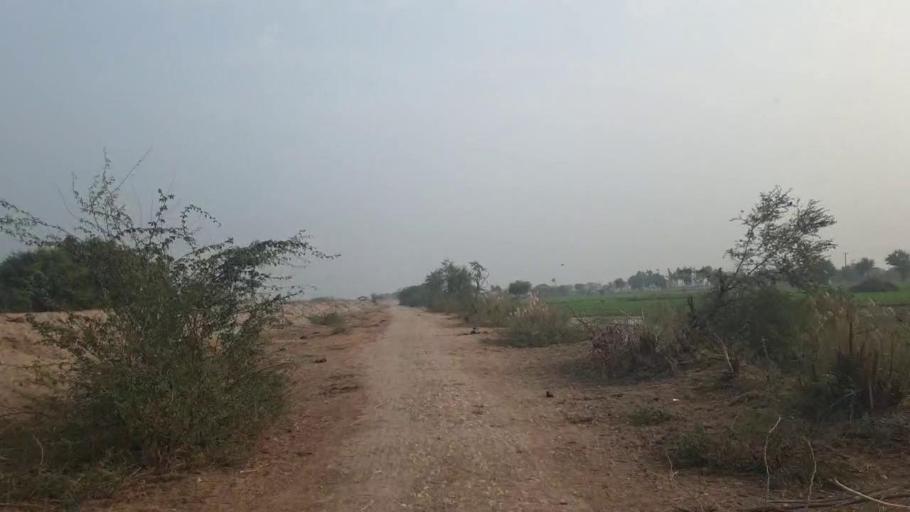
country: PK
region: Sindh
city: Berani
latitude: 25.8096
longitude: 68.7483
